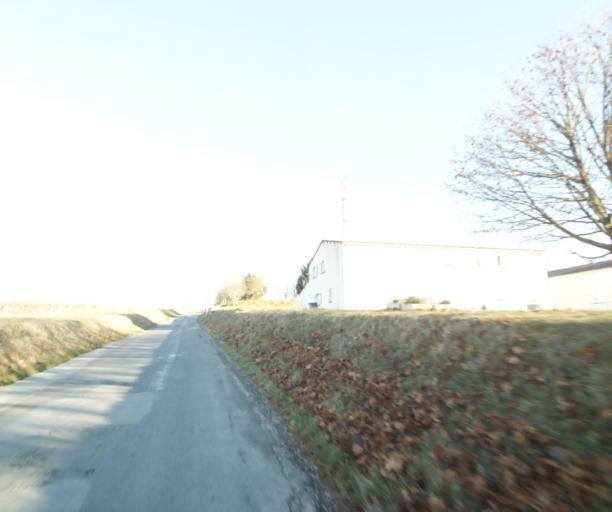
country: FR
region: Poitou-Charentes
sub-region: Departement de la Charente-Maritime
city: Cherac
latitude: 45.6995
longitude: -0.4370
